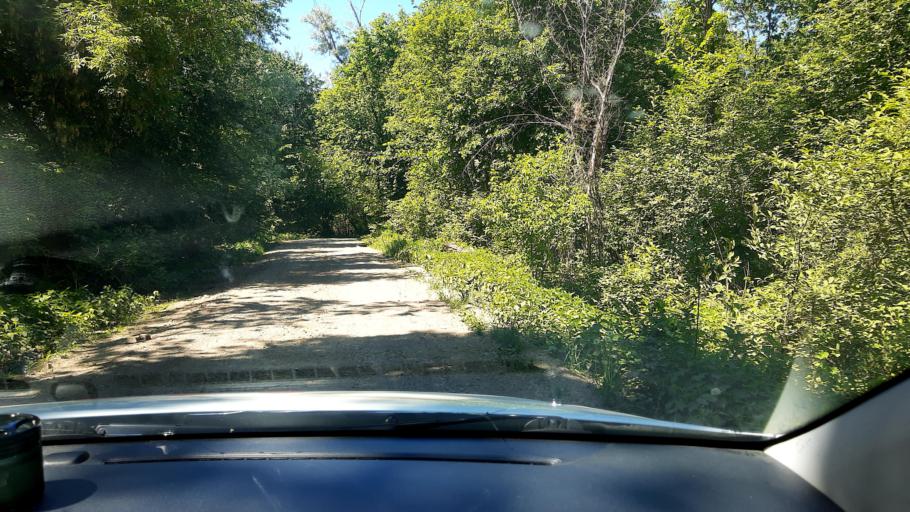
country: RU
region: Bashkortostan
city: Mikhaylovka
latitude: 54.7391
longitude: 55.8595
